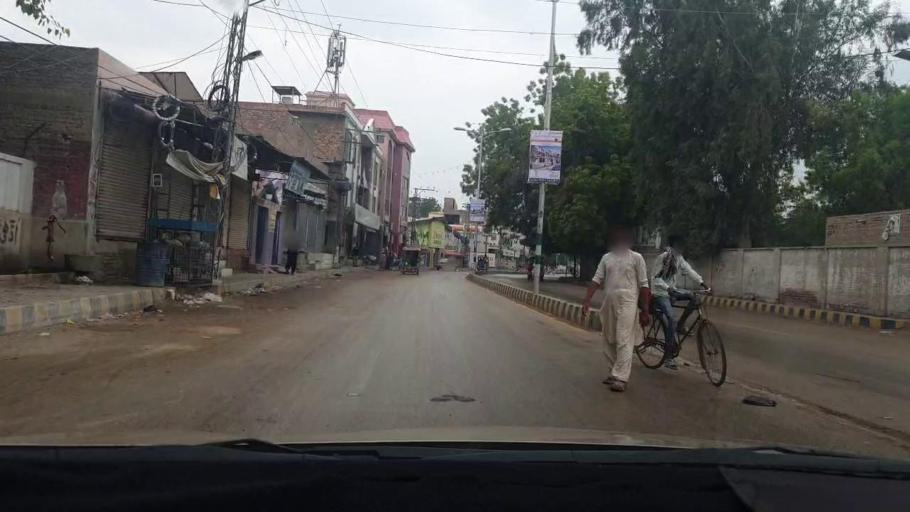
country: PK
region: Sindh
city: Larkana
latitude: 27.5571
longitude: 68.2094
